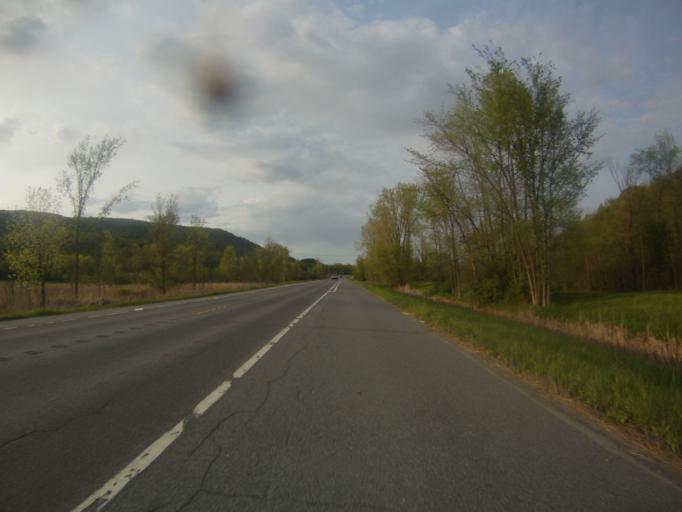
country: US
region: New York
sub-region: Essex County
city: Ticonderoga
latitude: 43.9050
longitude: -73.4266
